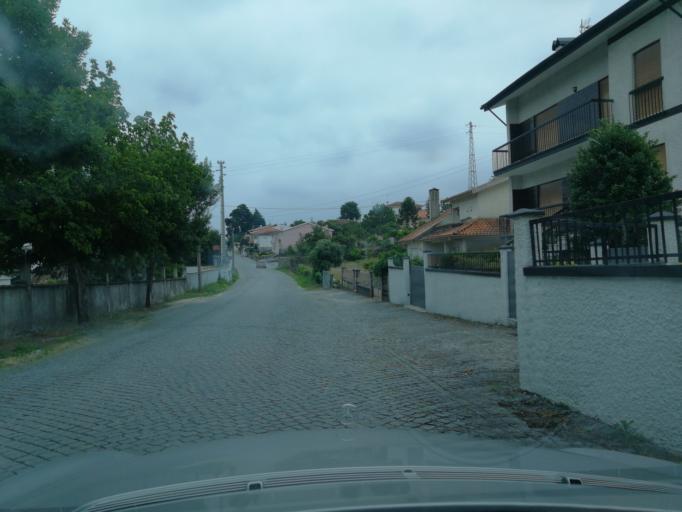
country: PT
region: Braga
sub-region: Braga
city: Adaufe
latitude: 41.6034
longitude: -8.4330
